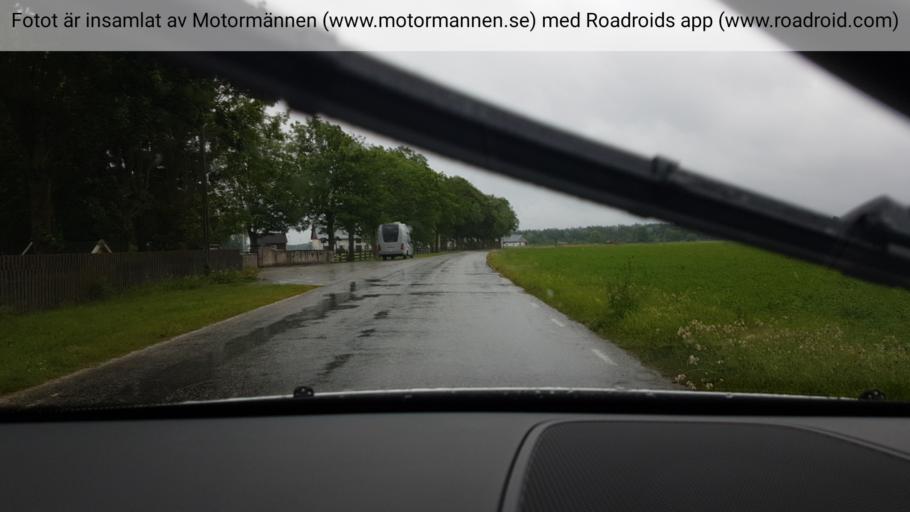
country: SE
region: Gotland
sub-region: Gotland
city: Slite
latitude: 57.5756
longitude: 18.7329
